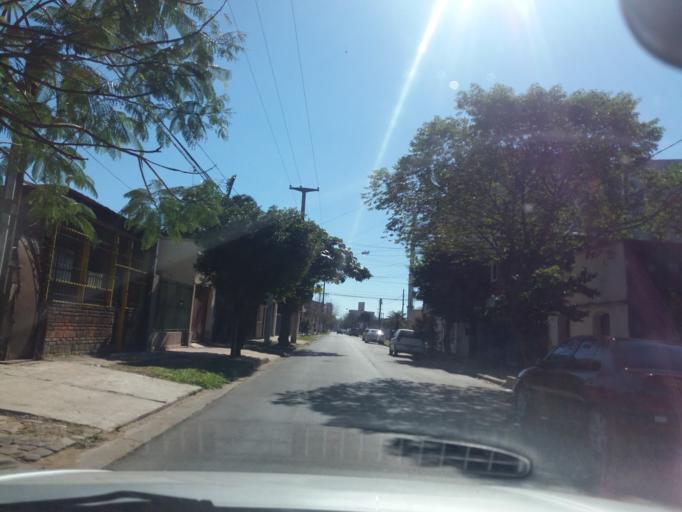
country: AR
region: Corrientes
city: Corrientes
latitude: -27.4817
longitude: -58.8439
